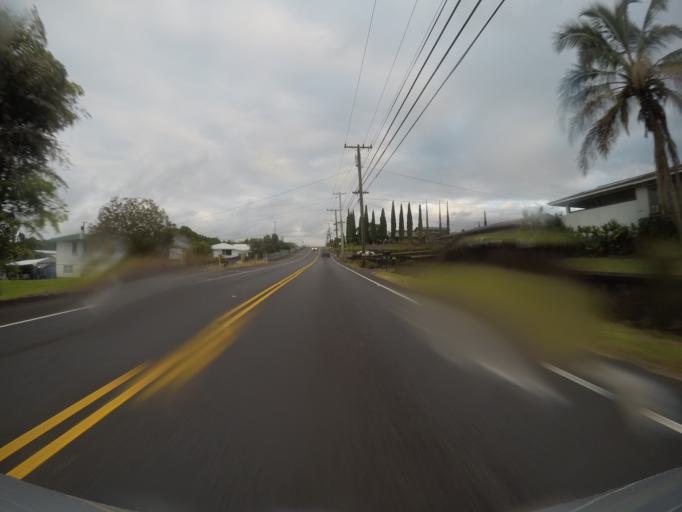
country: US
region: Hawaii
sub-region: Hawaii County
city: Hilo
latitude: 19.6875
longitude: -155.0901
